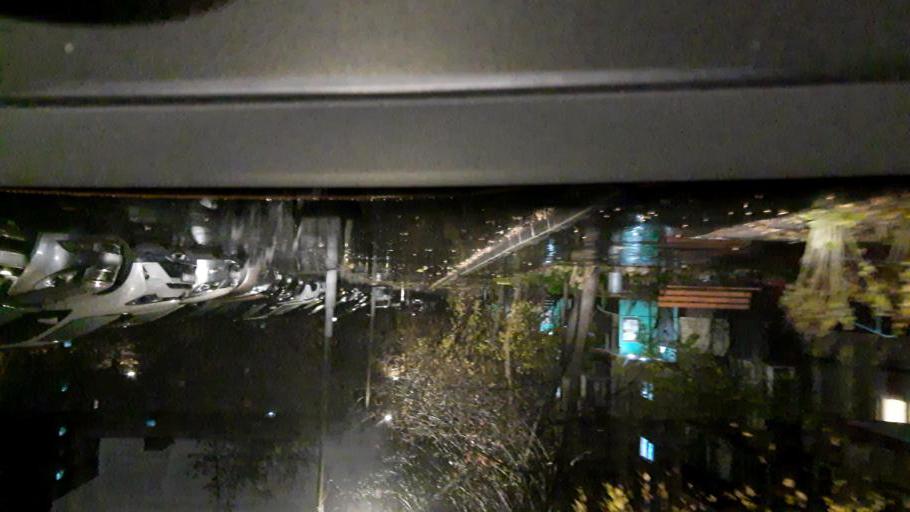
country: RU
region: Moscow
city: Bibirevo
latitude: 55.8935
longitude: 37.6063
